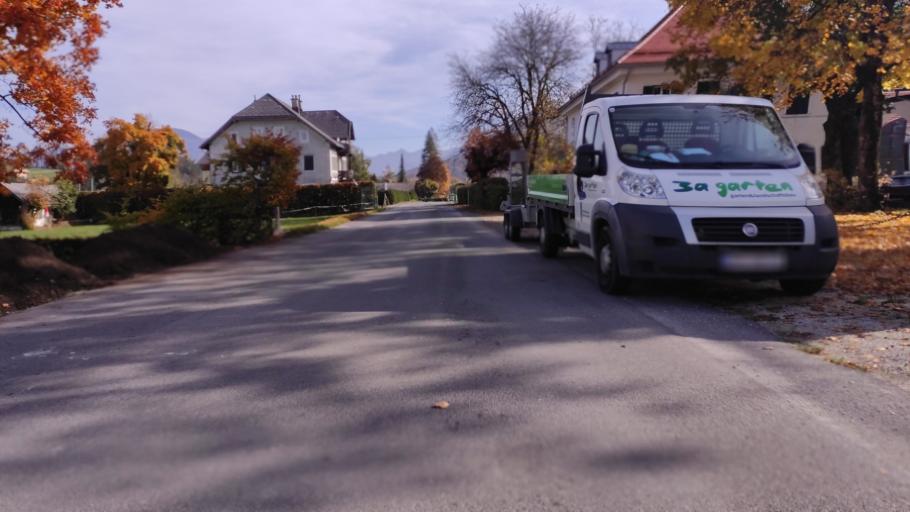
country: AT
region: Salzburg
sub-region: Politischer Bezirk Salzburg-Umgebung
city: Strobl
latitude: 47.7151
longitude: 13.5357
